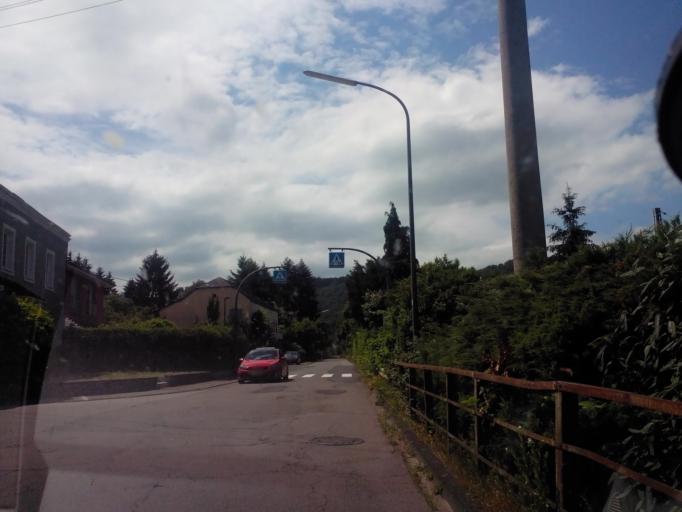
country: DE
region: Rheinland-Pfalz
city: Saarburg
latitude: 49.6056
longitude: 6.5570
